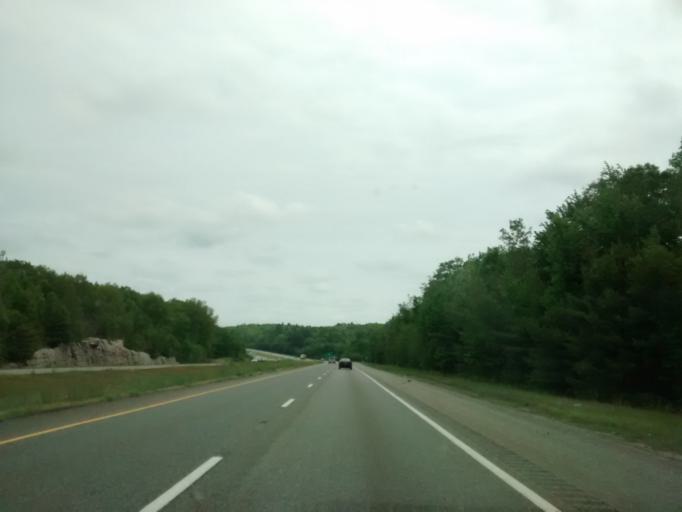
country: US
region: Massachusetts
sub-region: Worcester County
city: Uxbridge
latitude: 42.0375
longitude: -71.6224
